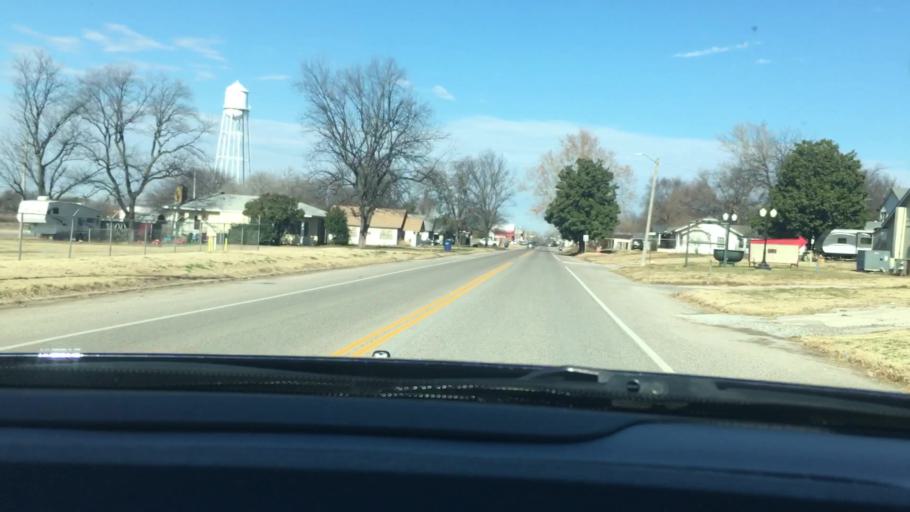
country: US
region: Oklahoma
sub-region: Garvin County
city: Wynnewood
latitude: 34.6372
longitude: -97.1693
